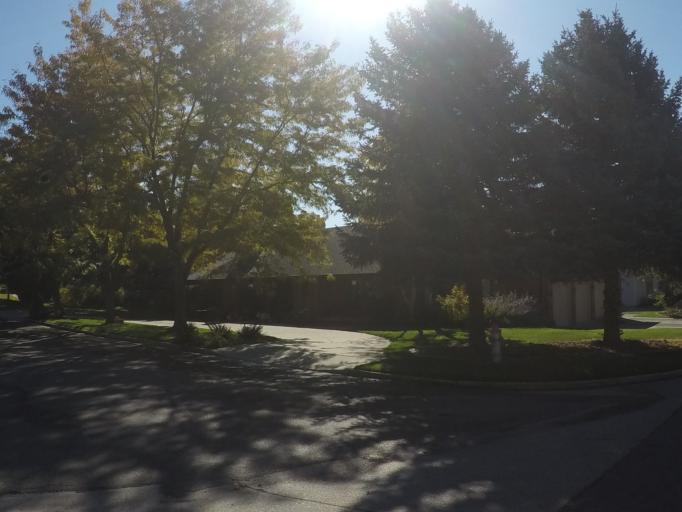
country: US
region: Montana
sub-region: Yellowstone County
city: Billings
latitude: 45.8014
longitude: -108.5900
